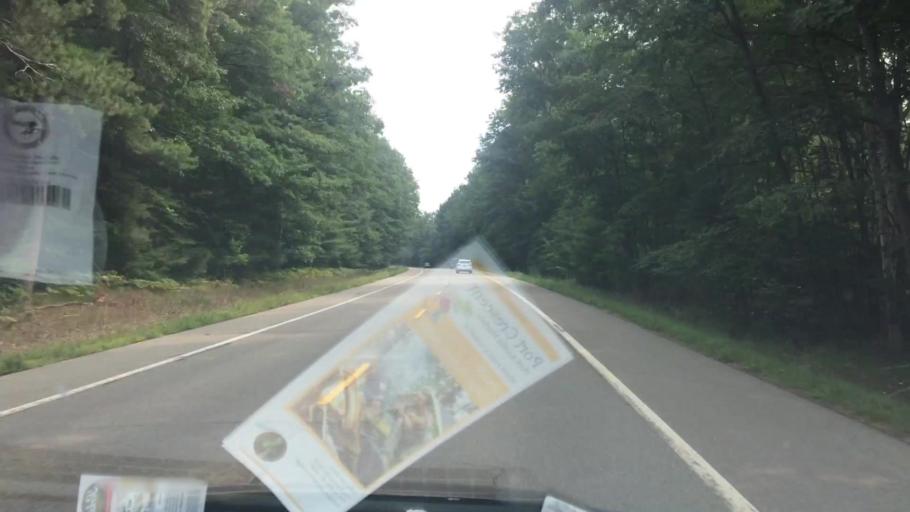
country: US
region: Michigan
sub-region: Huron County
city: Bad Axe
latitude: 43.9948
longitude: -83.0646
